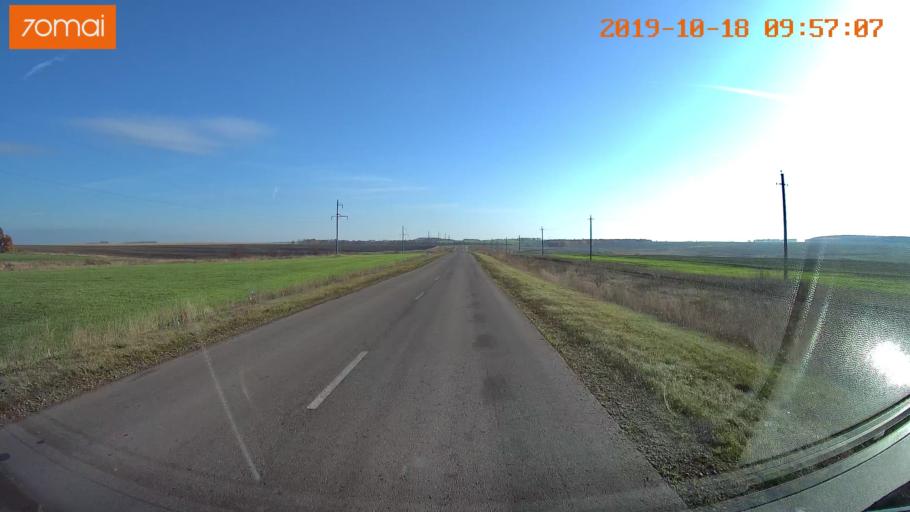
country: RU
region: Tula
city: Kurkino
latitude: 53.3759
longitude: 38.4081
